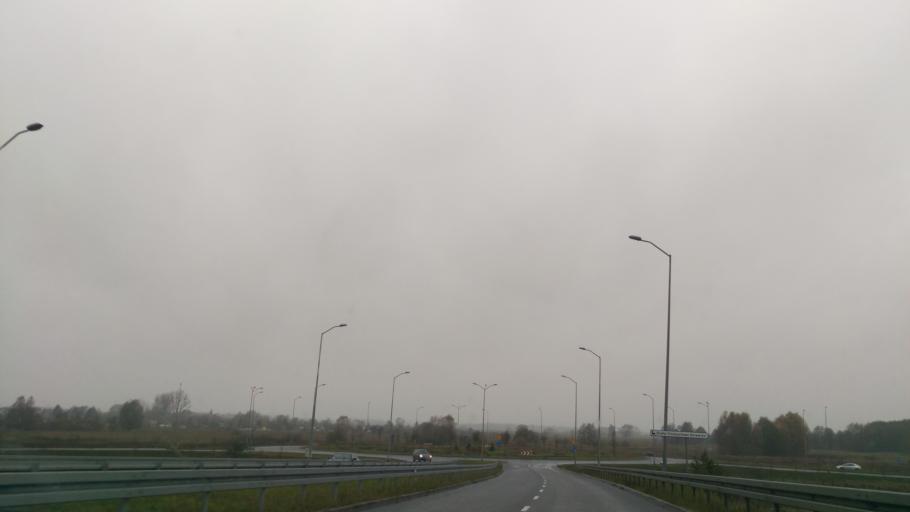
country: PL
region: West Pomeranian Voivodeship
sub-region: Szczecin
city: Szczecin
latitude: 53.4088
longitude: 14.7002
